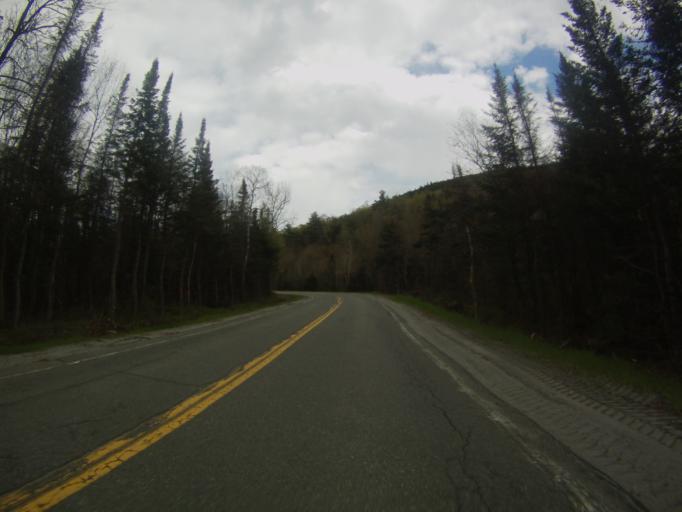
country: US
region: New York
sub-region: Essex County
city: Mineville
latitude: 44.0909
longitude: -73.5810
